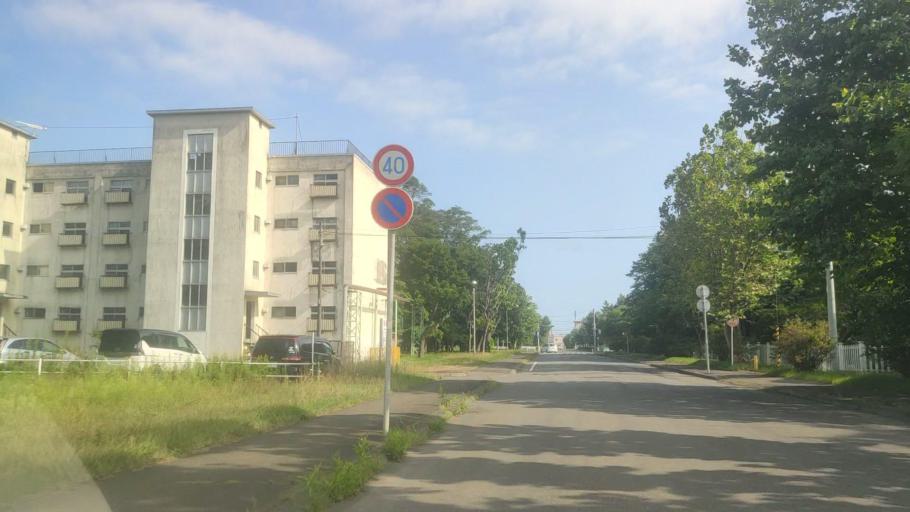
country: JP
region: Hokkaido
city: Tomakomai
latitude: 42.6373
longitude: 141.5943
